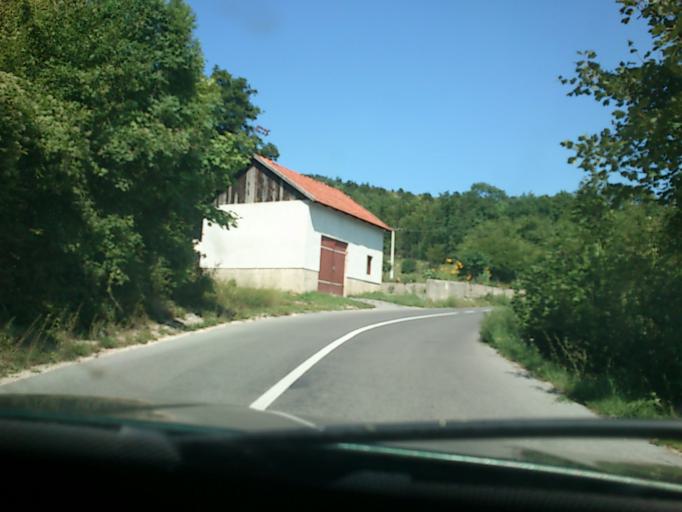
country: HR
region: Licko-Senjska
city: Otocac
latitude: 44.8197
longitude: 15.0789
